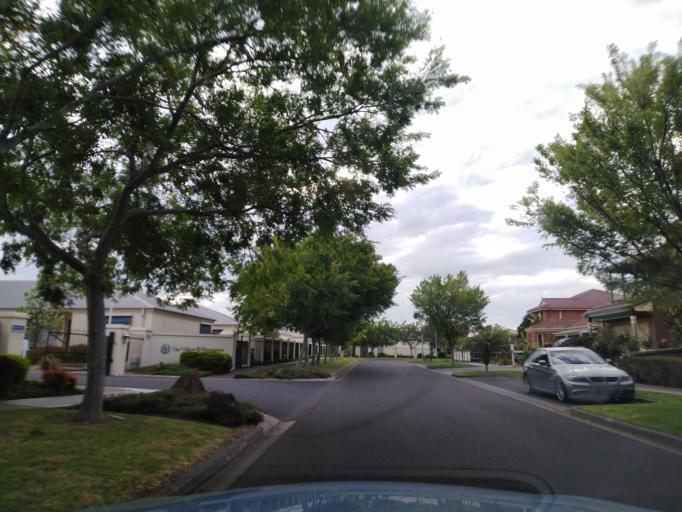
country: AU
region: Victoria
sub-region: Hobsons Bay
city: Williamstown North
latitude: -37.8589
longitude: 144.8770
